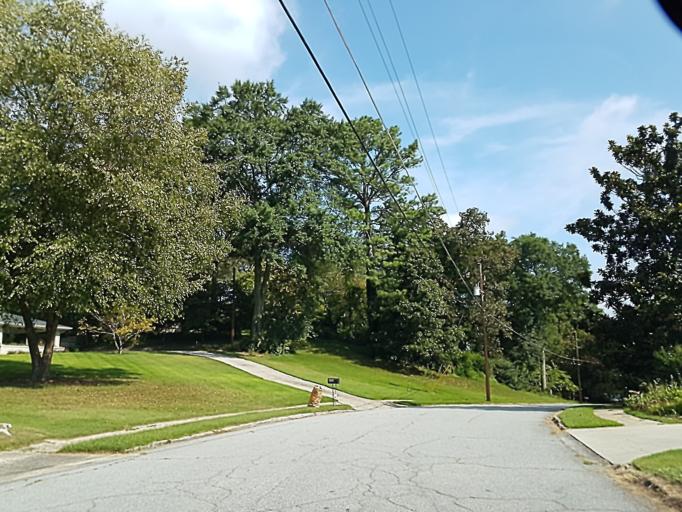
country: US
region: Georgia
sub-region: DeKalb County
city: North Druid Hills
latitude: 33.8355
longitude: -84.3095
